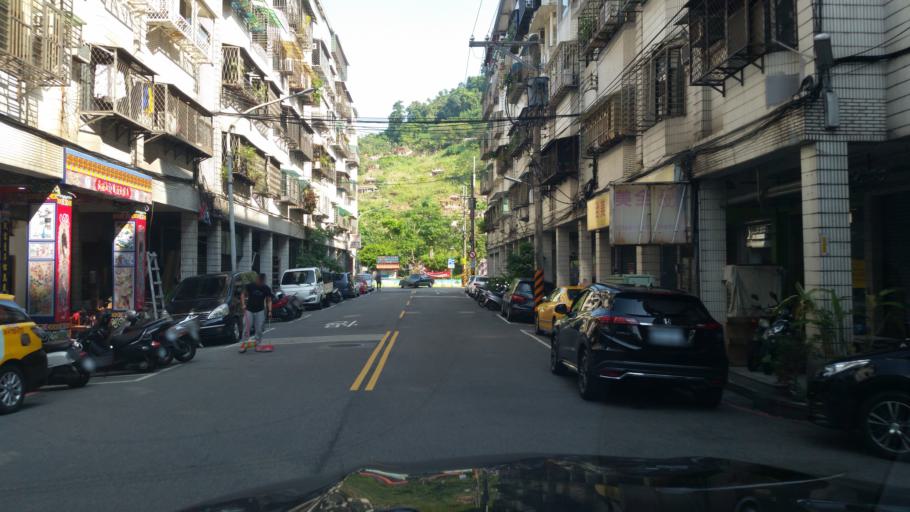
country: TW
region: Taipei
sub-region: Taipei
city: Banqiao
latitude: 24.9865
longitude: 121.5211
